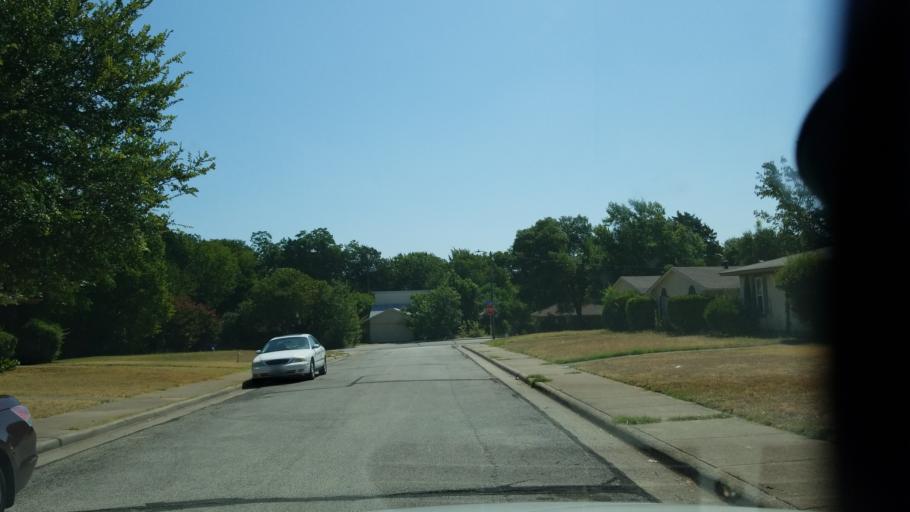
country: US
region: Texas
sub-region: Dallas County
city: Duncanville
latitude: 32.6413
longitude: -96.8972
